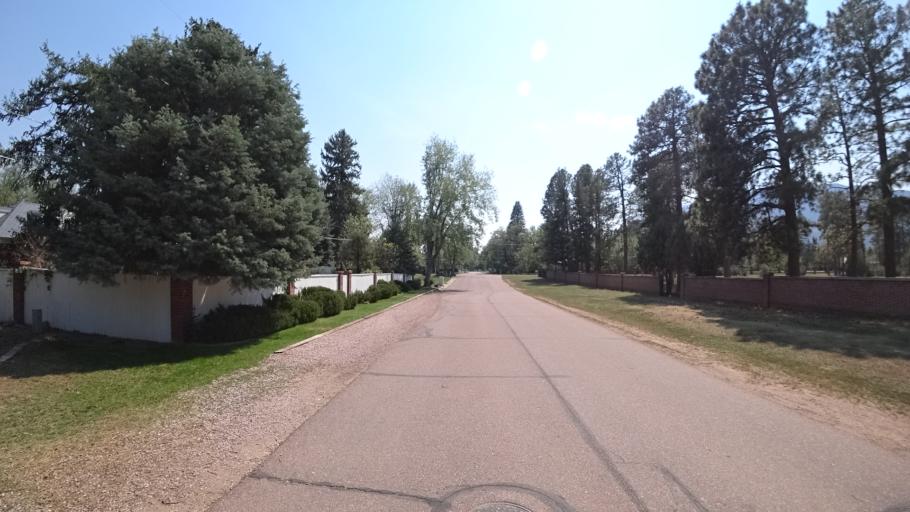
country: US
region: Colorado
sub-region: El Paso County
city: Colorado Springs
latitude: 38.7950
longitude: -104.8429
